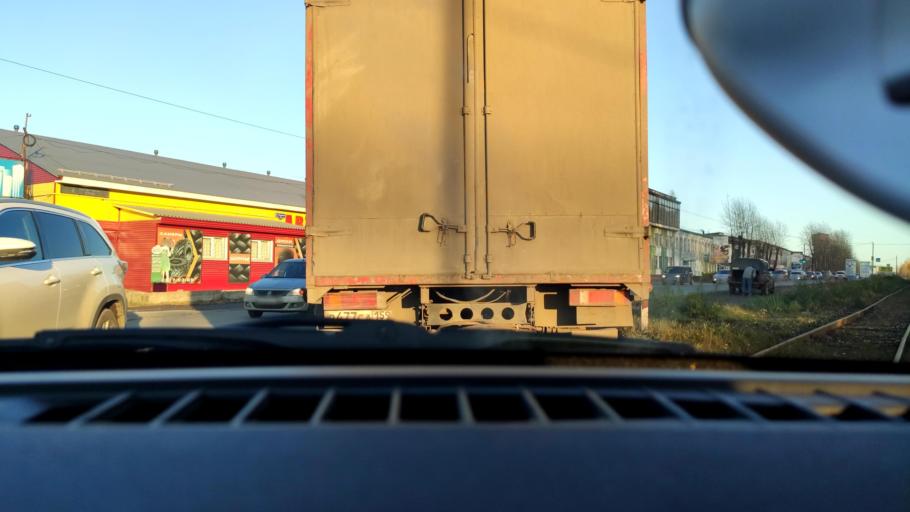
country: RU
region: Perm
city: Perm
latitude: 57.9573
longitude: 56.2137
